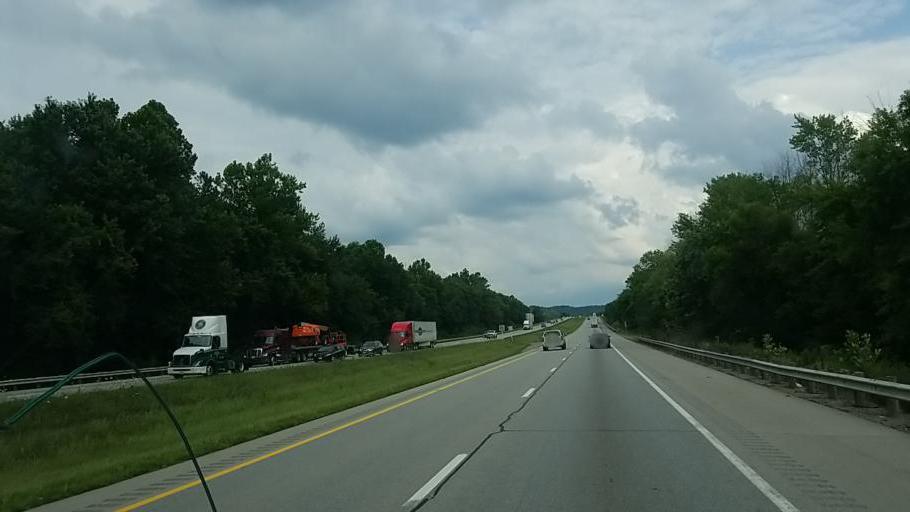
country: US
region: Ohio
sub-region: Guernsey County
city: Byesville
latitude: 40.0040
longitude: -81.5236
